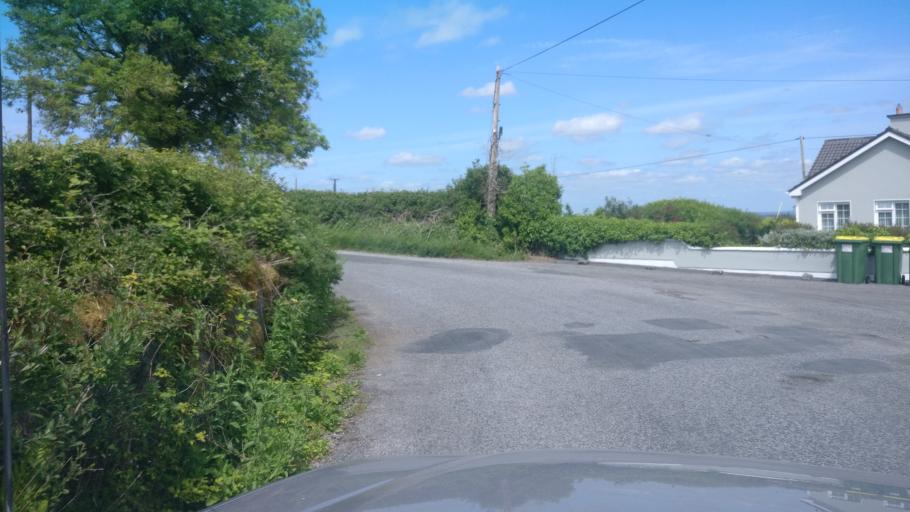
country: IE
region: Connaught
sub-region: County Galway
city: Loughrea
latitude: 53.1601
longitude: -8.6370
